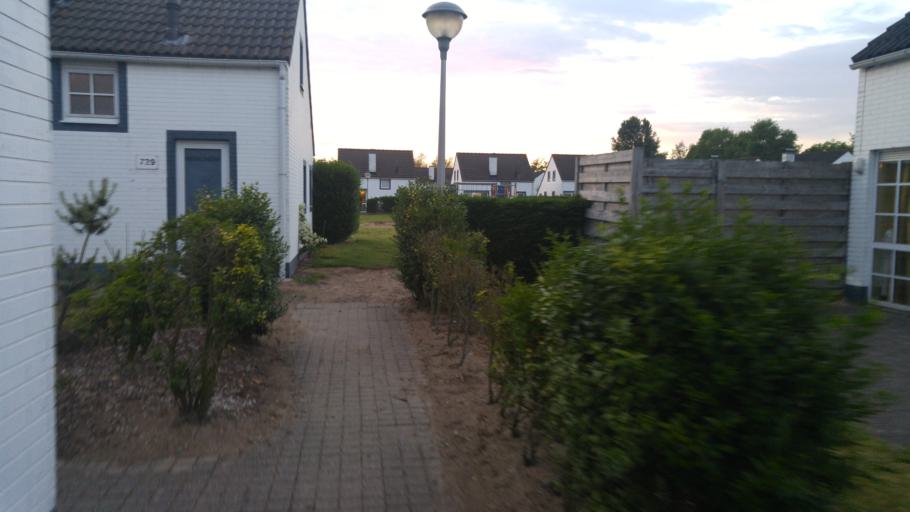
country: BE
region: Flanders
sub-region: Provincie West-Vlaanderen
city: Nieuwpoort
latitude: 51.1270
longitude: 2.7121
